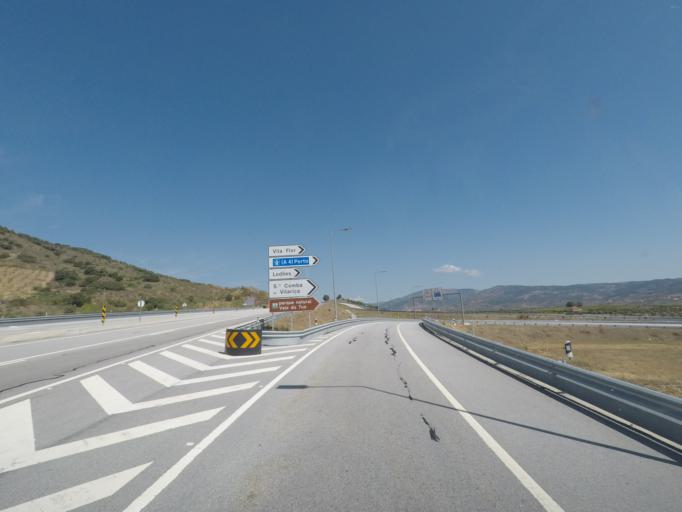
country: PT
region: Braganca
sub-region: Braganca Municipality
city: Vila Flor
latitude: 41.3251
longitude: -7.0793
